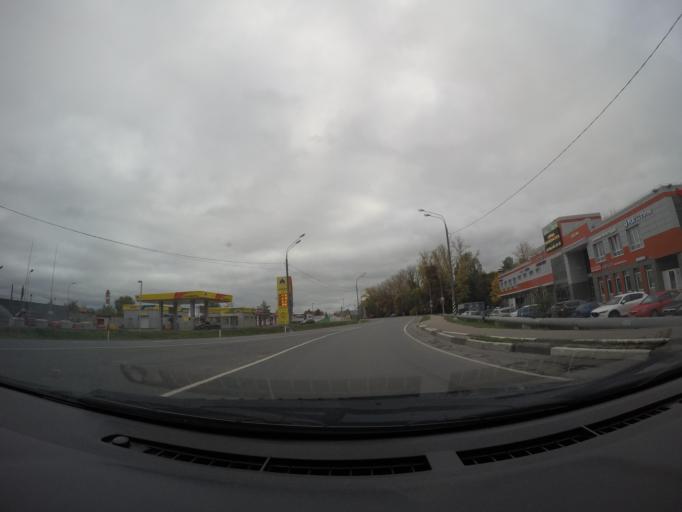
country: RU
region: Moskovskaya
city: Ruza
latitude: 55.7098
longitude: 36.2040
